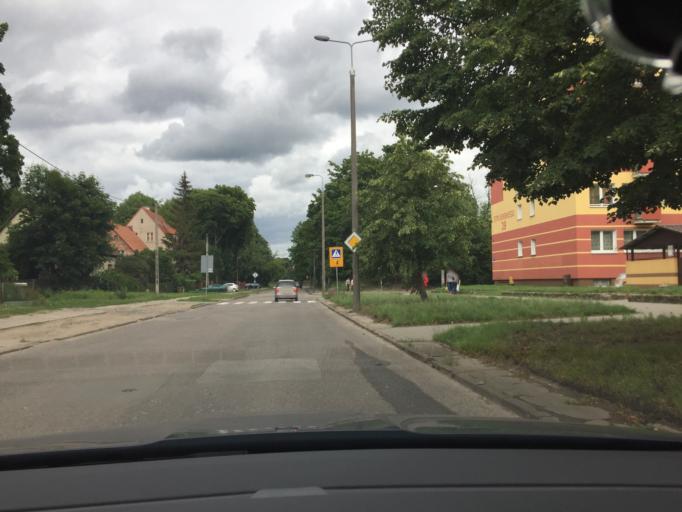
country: PL
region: Pomeranian Voivodeship
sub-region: Gdansk
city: Gdansk
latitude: 54.3616
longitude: 18.7180
